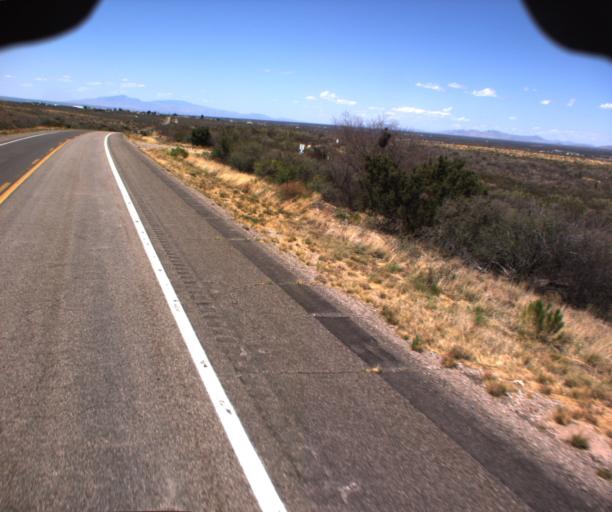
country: US
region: Arizona
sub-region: Cochise County
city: Tombstone
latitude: 31.6913
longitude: -110.0385
